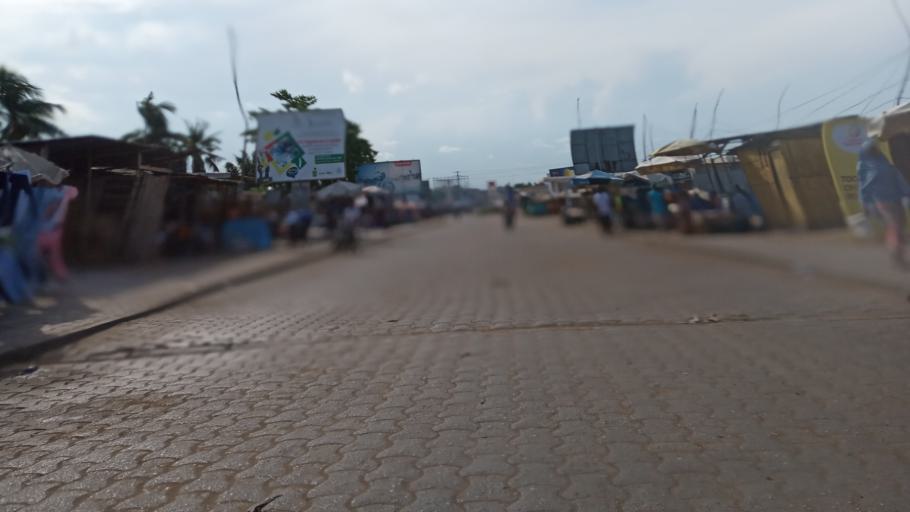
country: TG
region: Maritime
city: Lome
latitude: 6.1542
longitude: 1.2684
